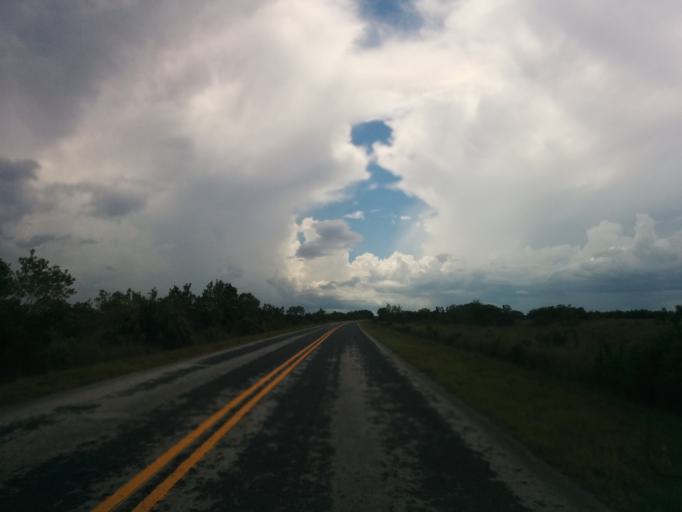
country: US
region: Florida
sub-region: Miami-Dade County
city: Florida City
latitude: 25.4328
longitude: -80.7418
